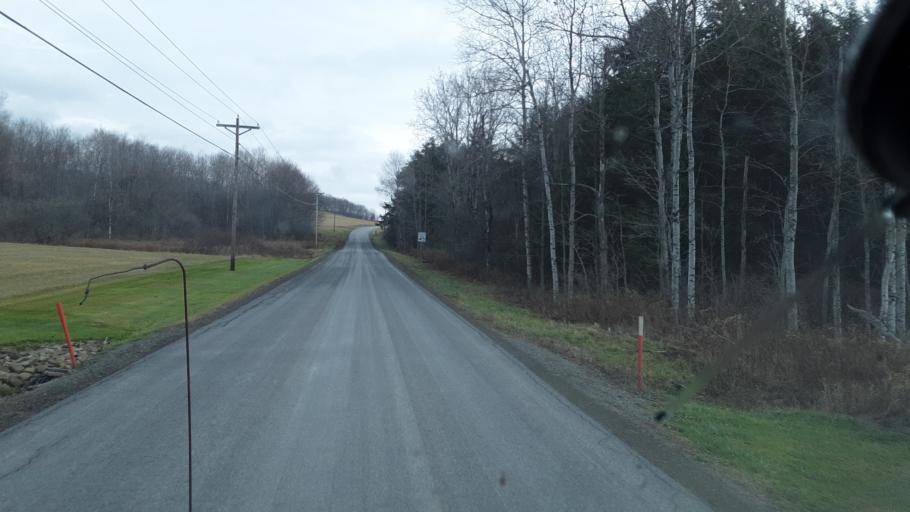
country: US
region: Pennsylvania
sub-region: Potter County
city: Galeton
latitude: 41.8877
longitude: -77.7746
